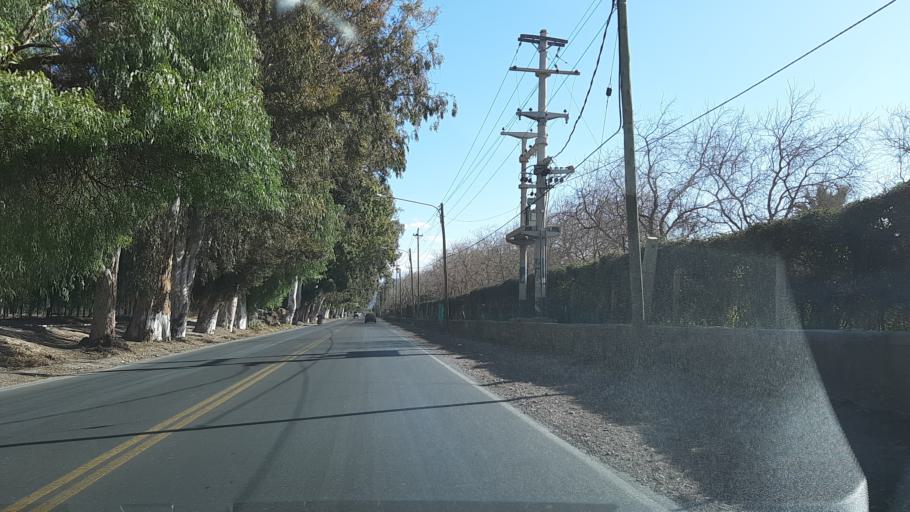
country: AR
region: San Juan
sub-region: Departamento de Rivadavia
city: Rivadavia
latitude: -31.5389
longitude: -68.6013
